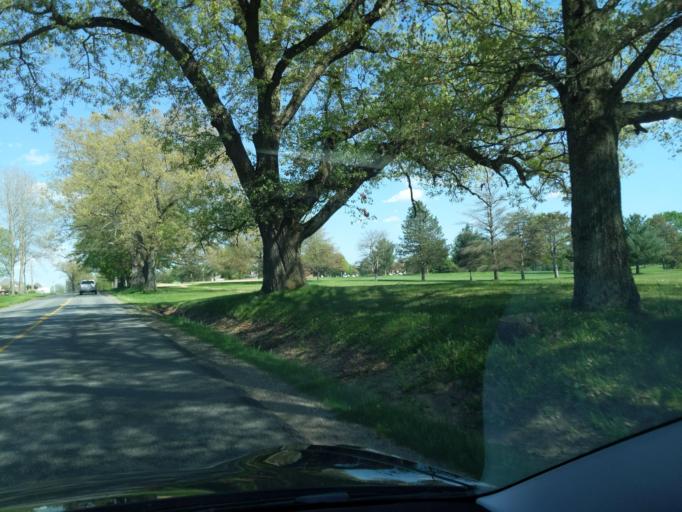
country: US
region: Michigan
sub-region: Kent County
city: Caledonia
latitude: 42.7979
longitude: -85.4456
